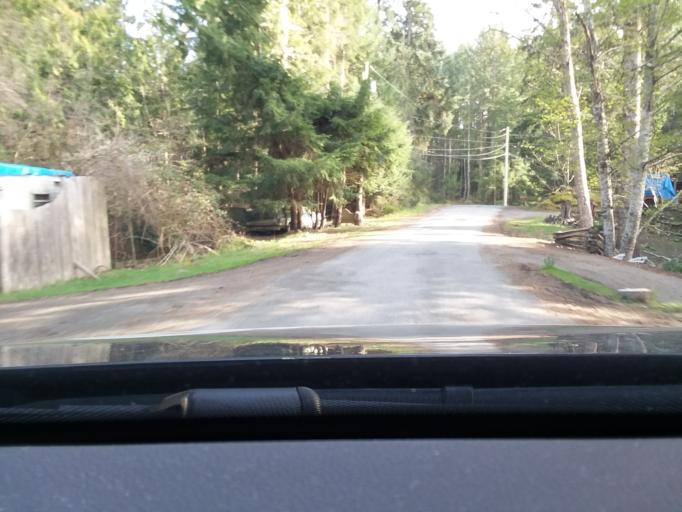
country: CA
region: British Columbia
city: North Saanich
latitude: 48.7728
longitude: -123.2962
